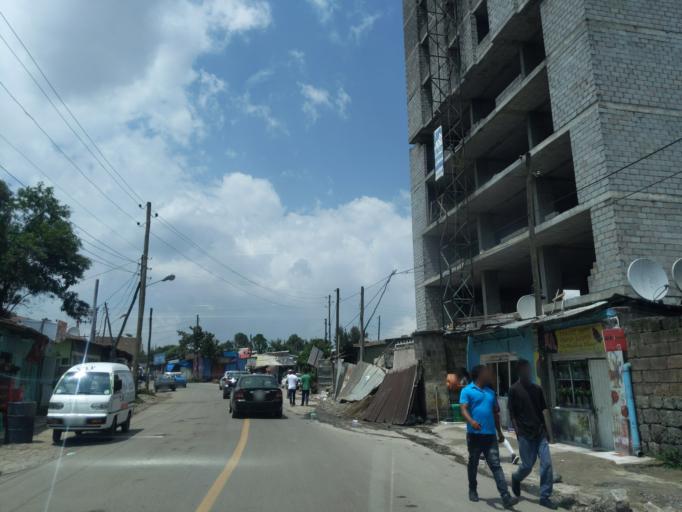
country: ET
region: Adis Abeba
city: Addis Ababa
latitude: 9.0174
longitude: 38.7756
